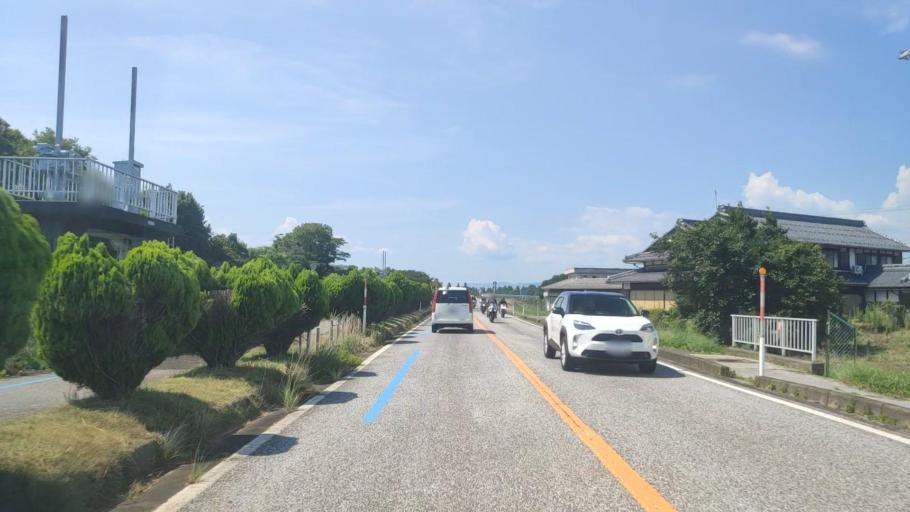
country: JP
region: Shiga Prefecture
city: Nagahama
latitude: 35.4030
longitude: 136.2153
